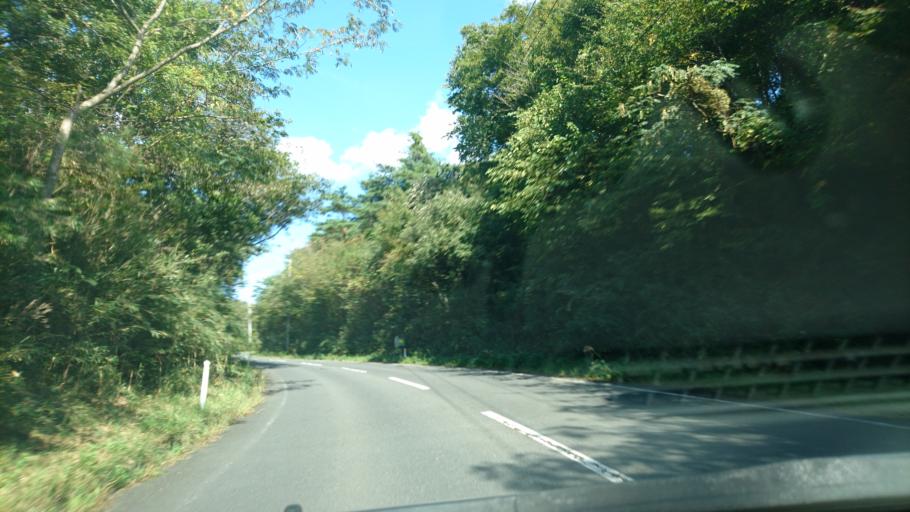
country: JP
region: Iwate
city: Ichinoseki
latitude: 38.8466
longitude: 141.0325
